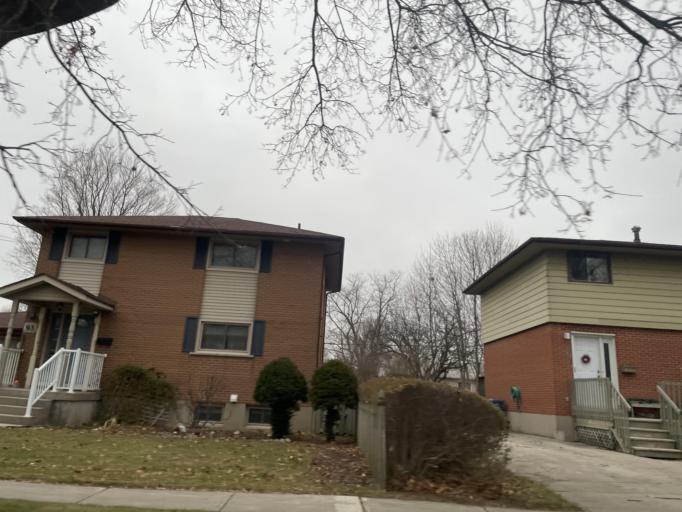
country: CA
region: Ontario
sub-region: Wellington County
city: Guelph
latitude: 43.5417
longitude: -80.2722
